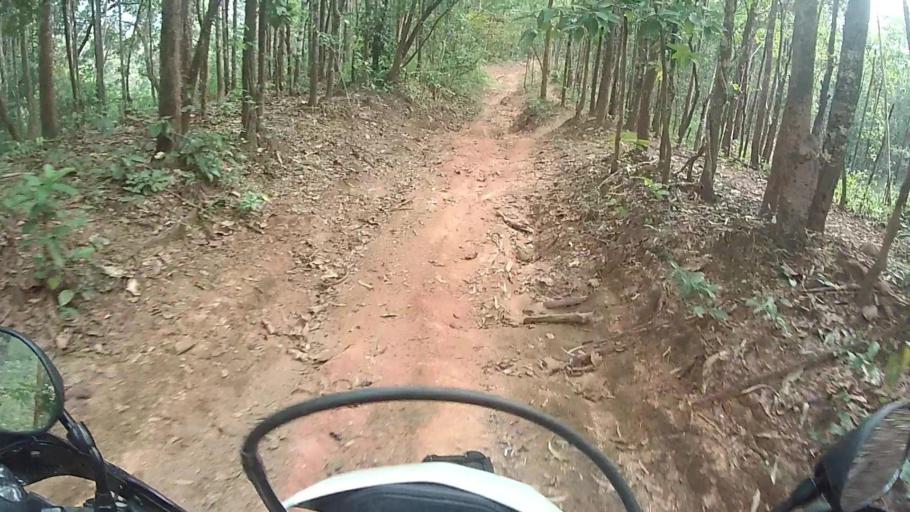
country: TH
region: Chiang Mai
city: Mae On
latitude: 18.7284
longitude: 99.2829
